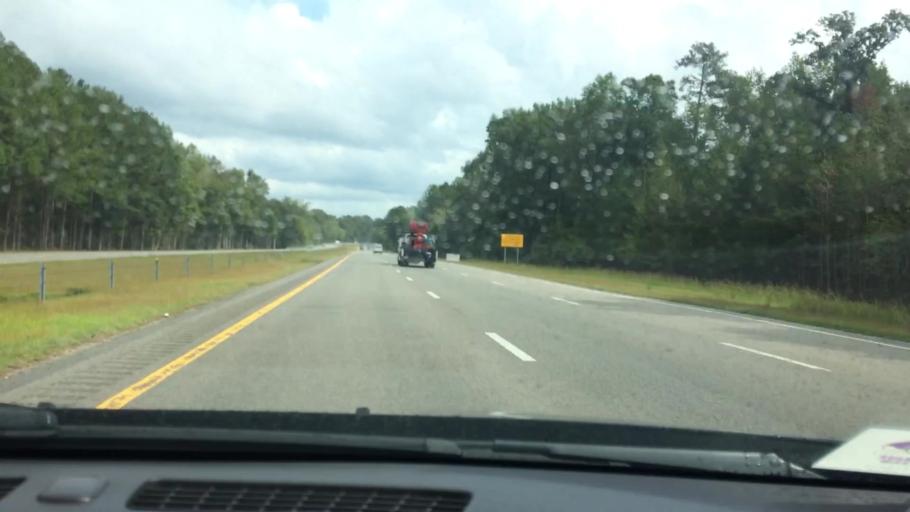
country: US
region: North Carolina
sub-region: Wilson County
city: Wilson
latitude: 35.6766
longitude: -77.8531
